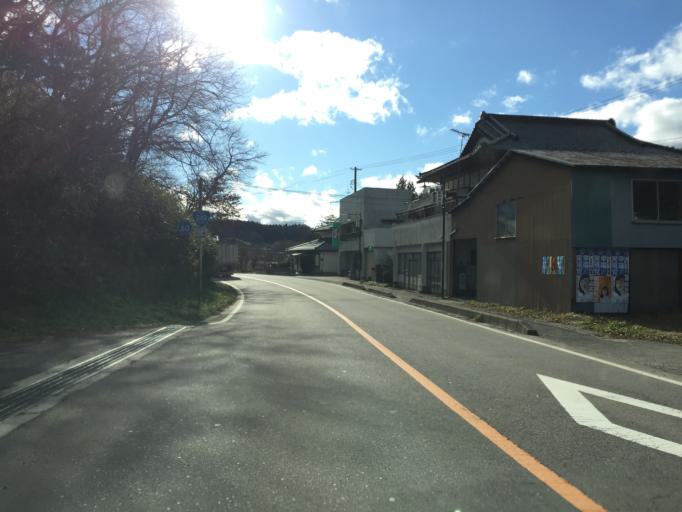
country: JP
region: Fukushima
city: Funehikimachi-funehiki
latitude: 37.4912
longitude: 140.5757
